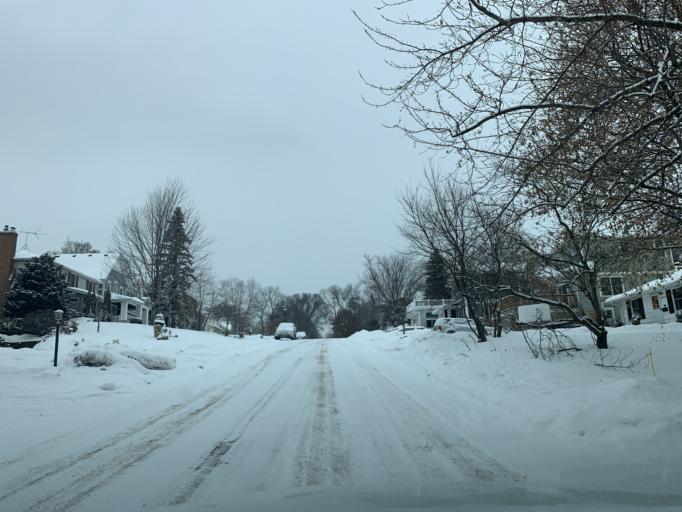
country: US
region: Minnesota
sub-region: Hennepin County
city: Saint Louis Park
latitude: 44.9289
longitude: -93.3367
